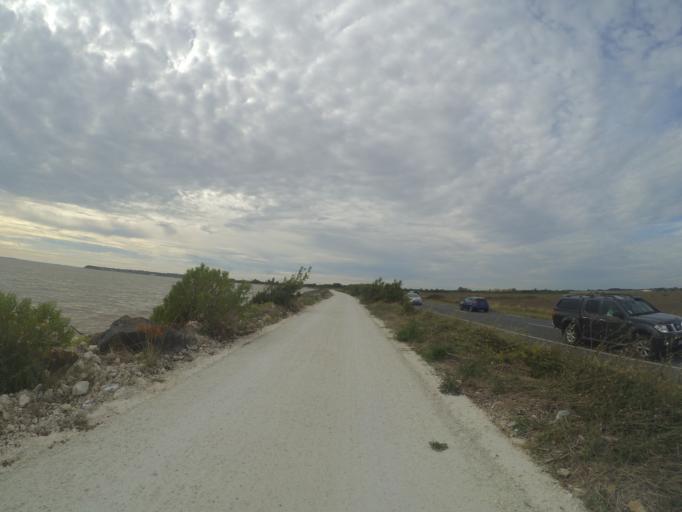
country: FR
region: Poitou-Charentes
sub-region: Departement de la Charente-Maritime
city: Meschers-sur-Gironde
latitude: 45.5464
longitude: -0.9121
